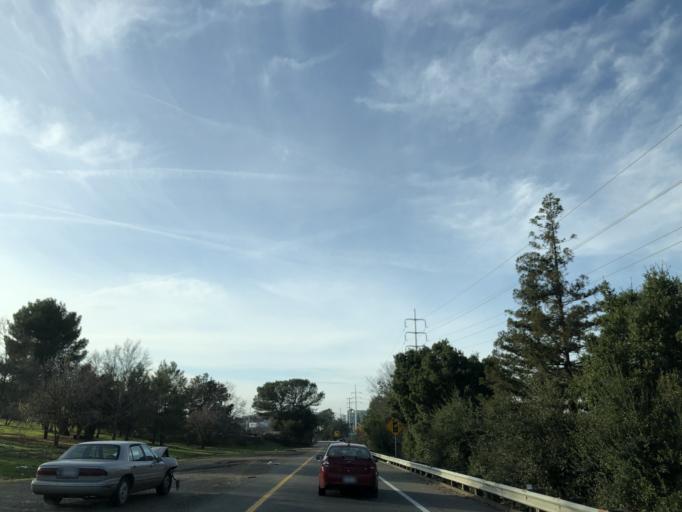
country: US
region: California
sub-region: Sacramento County
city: Sacramento
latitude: 38.5614
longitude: -121.4608
